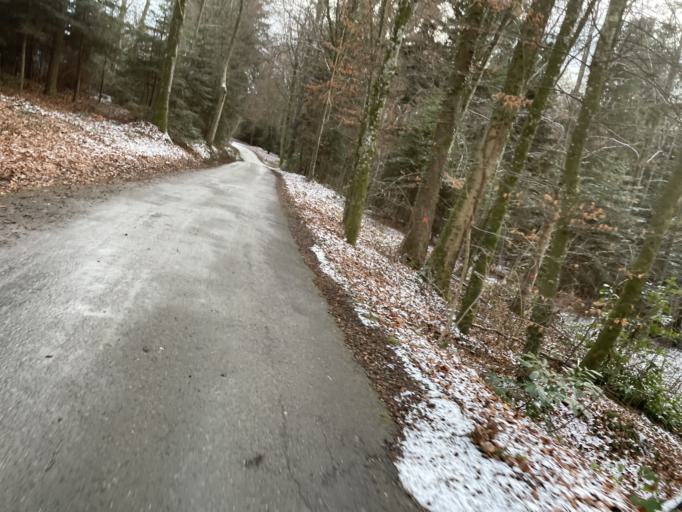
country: CH
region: Lucerne
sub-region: Entlebuch District
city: Oberdiessbach
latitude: 46.8423
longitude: 7.6026
